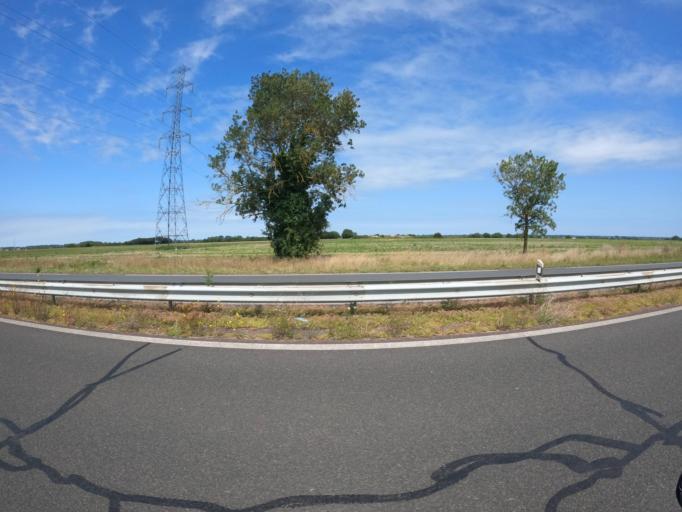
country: FR
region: Poitou-Charentes
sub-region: Departement des Deux-Sevres
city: Frontenay-Rohan-Rohan
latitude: 46.2516
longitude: -0.5526
